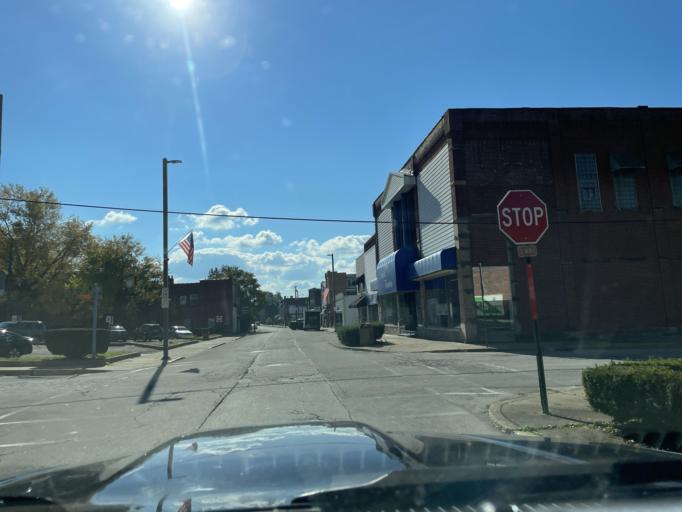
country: US
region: Pennsylvania
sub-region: Westmoreland County
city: Arnold
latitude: 40.5776
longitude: -79.7680
